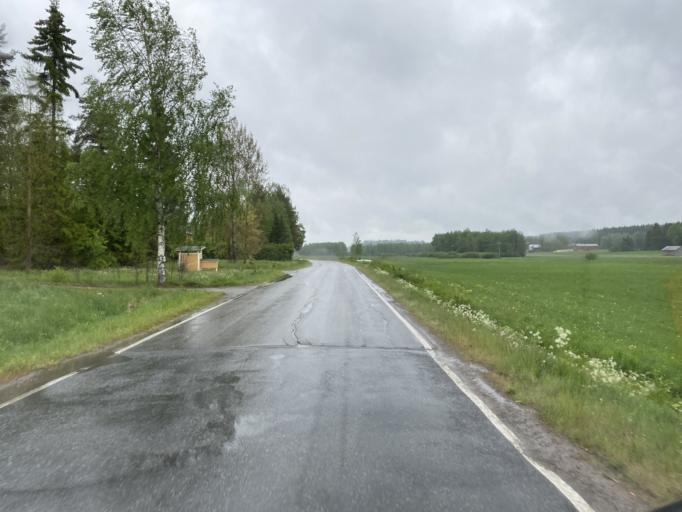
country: FI
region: Haeme
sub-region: Forssa
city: Humppila
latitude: 61.0422
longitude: 23.3953
